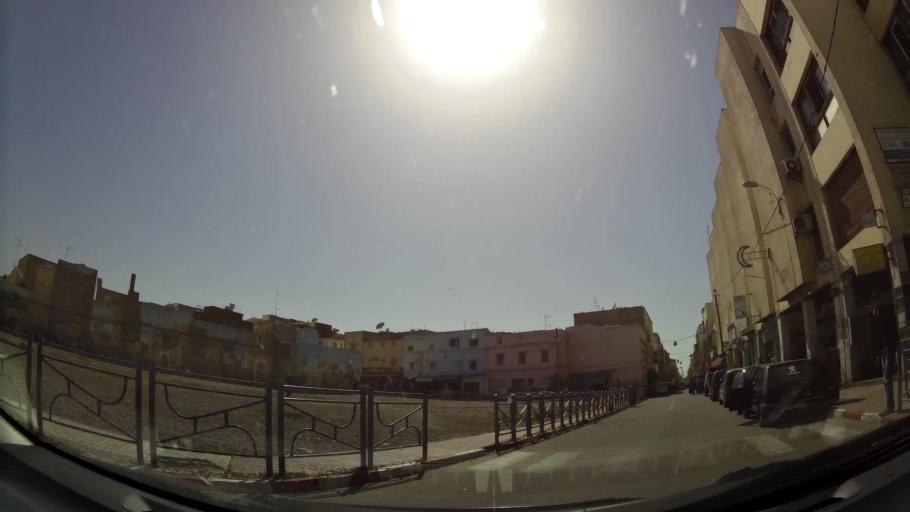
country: MA
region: Souss-Massa-Draa
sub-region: Inezgane-Ait Mellou
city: Inezgane
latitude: 30.3583
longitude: -9.5336
